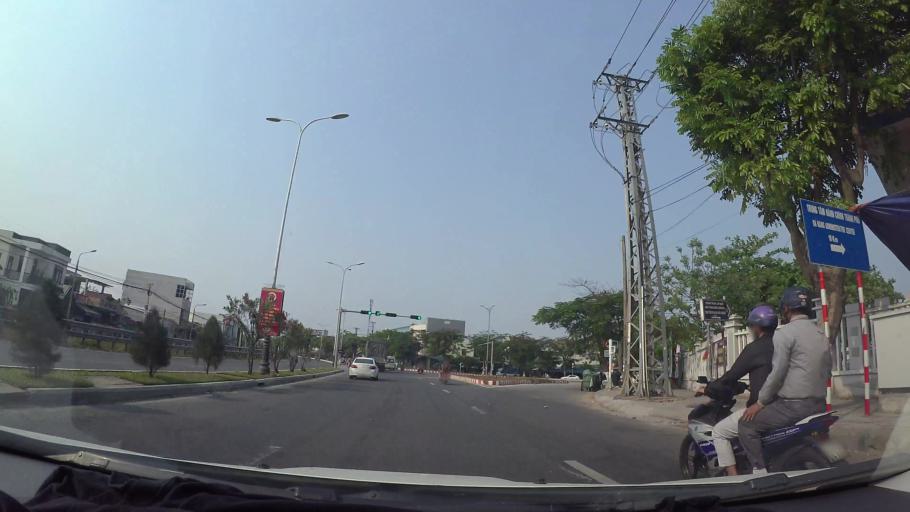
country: VN
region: Da Nang
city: Cam Le
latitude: 16.0197
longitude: 108.1940
